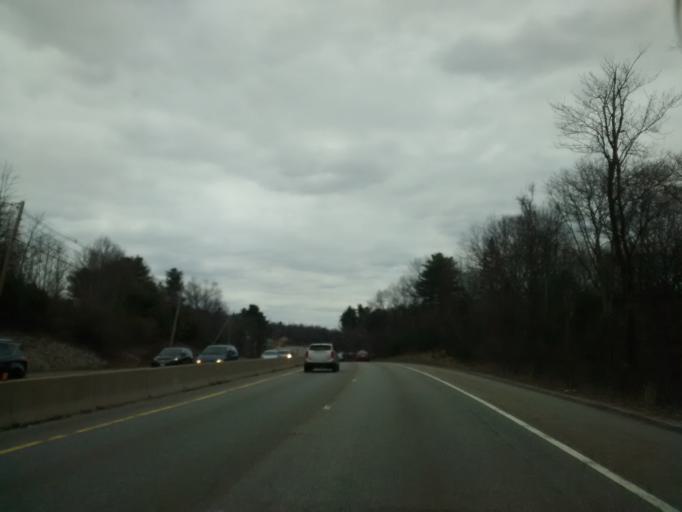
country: US
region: Massachusetts
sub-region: Worcester County
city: Charlton
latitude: 42.1449
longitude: -71.9538
